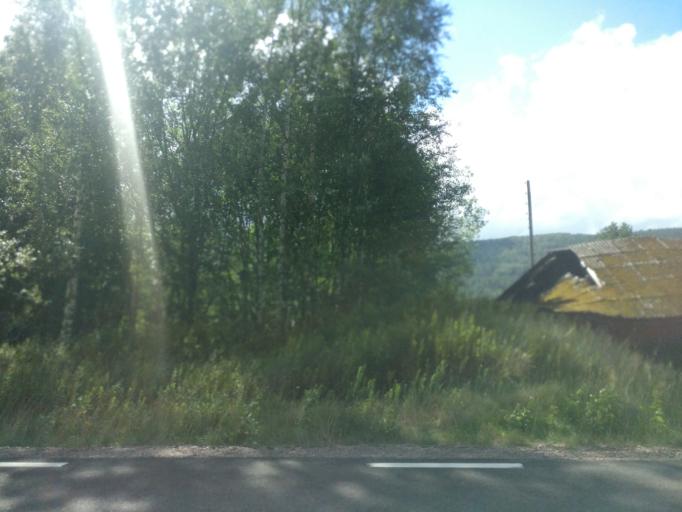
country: SE
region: Vaermland
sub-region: Hagfors Kommun
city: Ekshaerad
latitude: 60.3521
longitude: 13.3349
